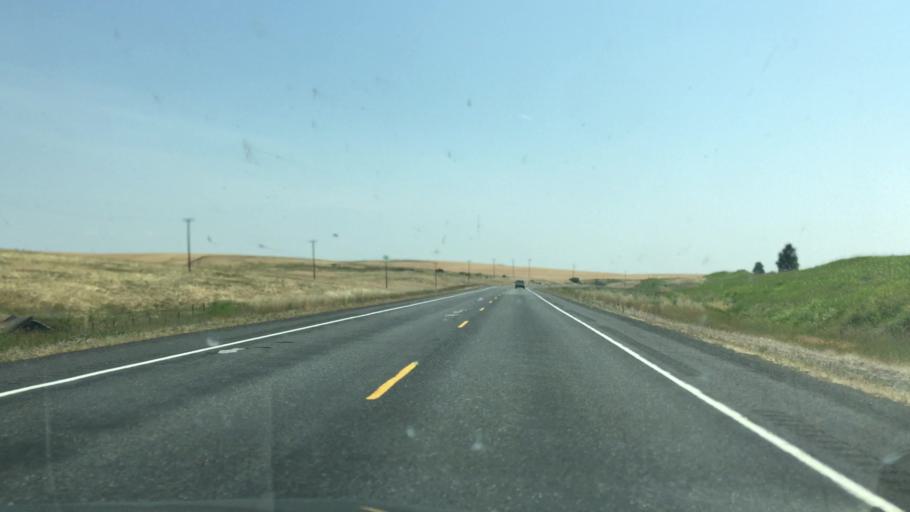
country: US
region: Idaho
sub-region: Lewis County
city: Nezperce
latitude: 46.2297
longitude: -116.4514
